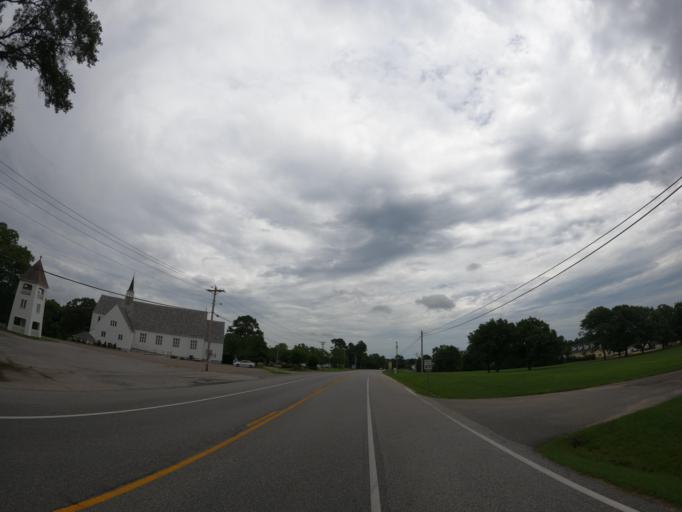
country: US
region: Maryland
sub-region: Saint Mary's County
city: California
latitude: 38.2388
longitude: -76.5098
